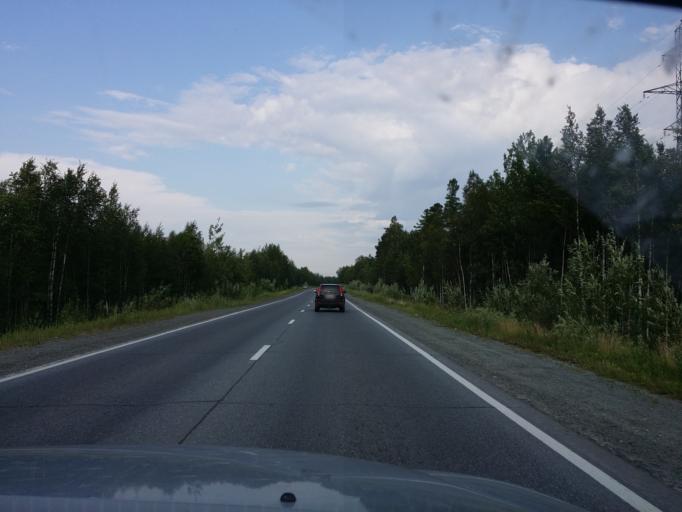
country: RU
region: Khanty-Mansiyskiy Avtonomnyy Okrug
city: Megion
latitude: 61.1274
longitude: 75.8035
